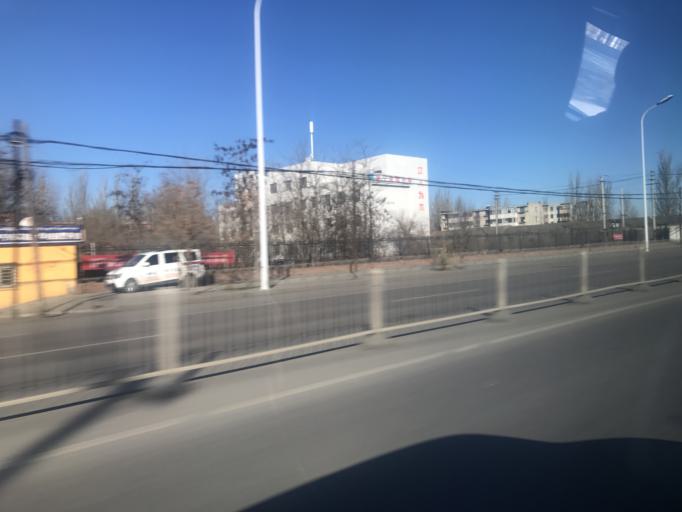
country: CN
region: Xinjiang Uygur Zizhiqu
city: Dadamtu
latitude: 43.9537
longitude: 81.3563
